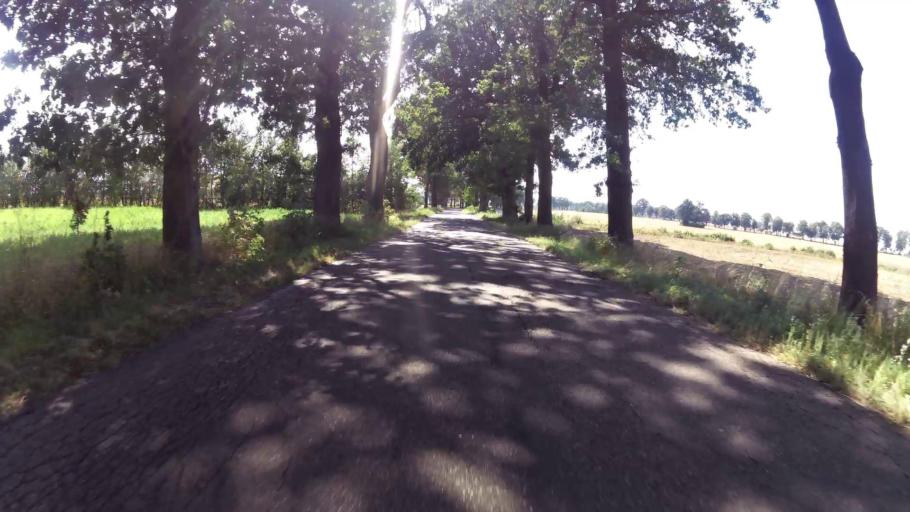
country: PL
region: West Pomeranian Voivodeship
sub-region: Powiat walecki
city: Walcz
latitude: 53.2114
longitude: 16.5009
